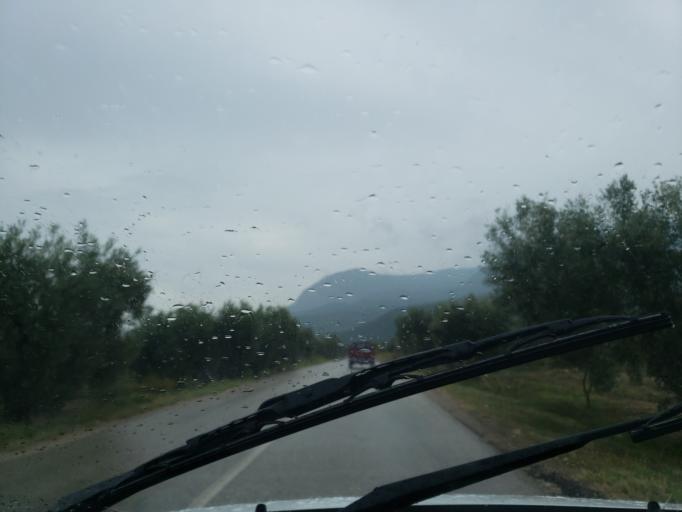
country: GR
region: Central Greece
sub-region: Nomos Fthiotidos
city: Anthili
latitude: 38.8034
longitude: 22.4559
